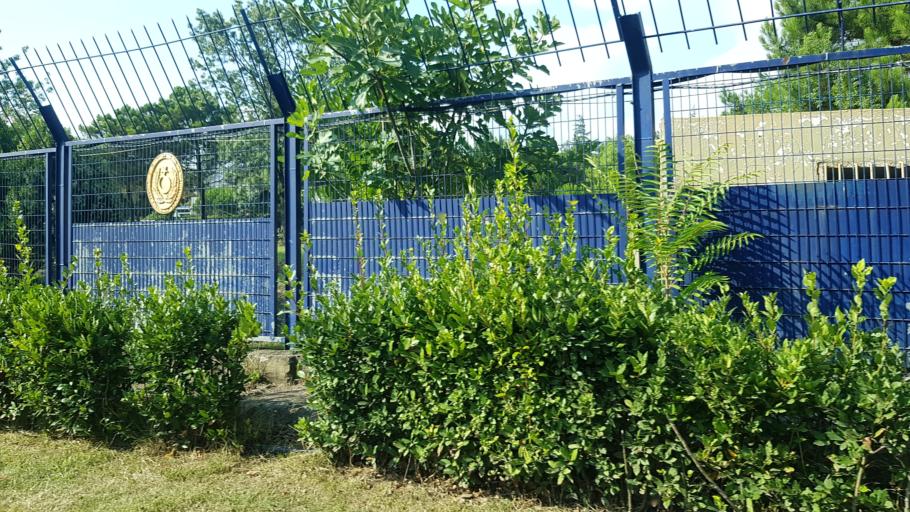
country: TR
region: Istanbul
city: Maltepe
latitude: 40.9196
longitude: 29.1729
